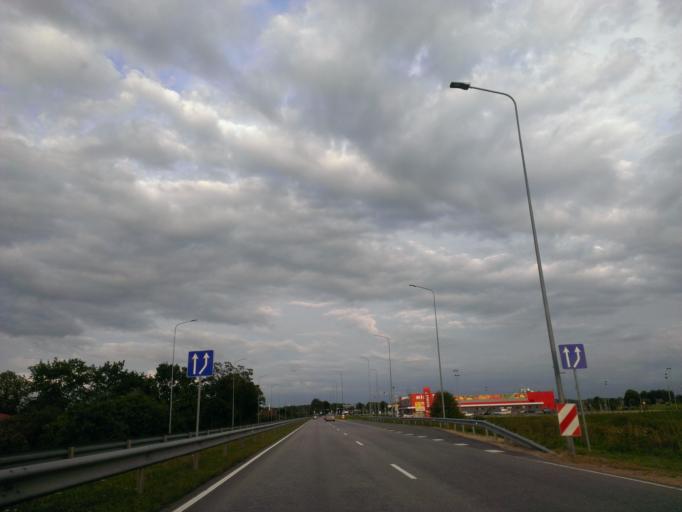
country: LV
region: Ogre
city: Ogre
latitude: 56.8184
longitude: 24.5715
